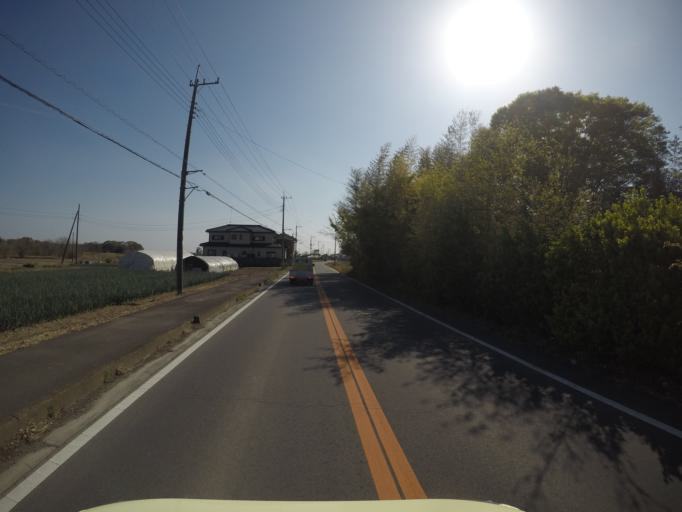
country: JP
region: Ibaraki
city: Yuki
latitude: 36.3648
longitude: 139.9059
